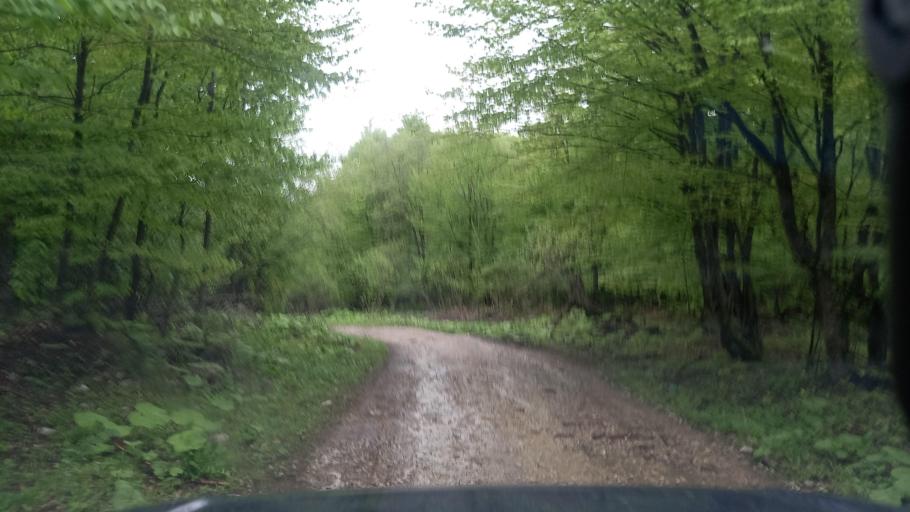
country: RU
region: Kabardino-Balkariya
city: Babugent
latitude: 43.2179
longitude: 43.5526
